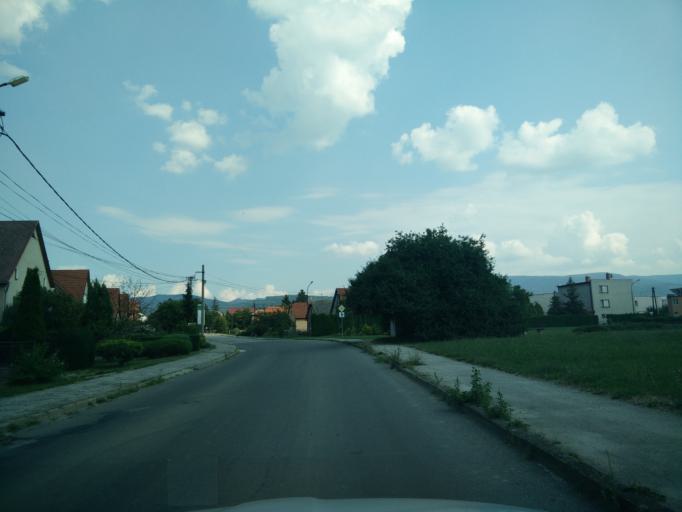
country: SK
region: Nitriansky
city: Prievidza
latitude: 48.7379
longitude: 18.6018
